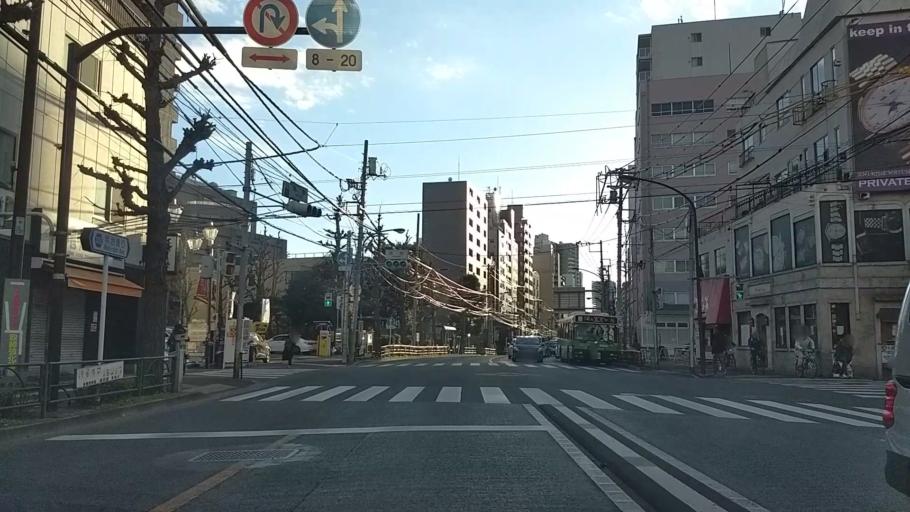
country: JP
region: Tokyo
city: Tokyo
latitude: 35.7425
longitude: 139.7265
